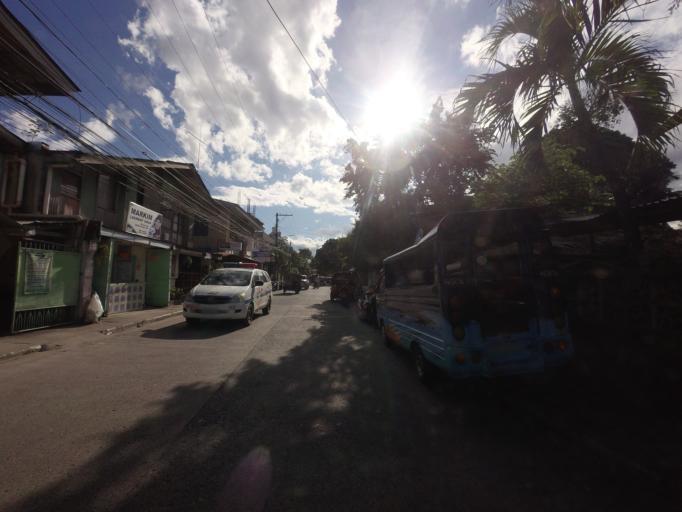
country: PH
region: Central Visayas
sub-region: Province of Negros Oriental
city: Dumaguete
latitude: 9.3060
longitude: 123.3021
